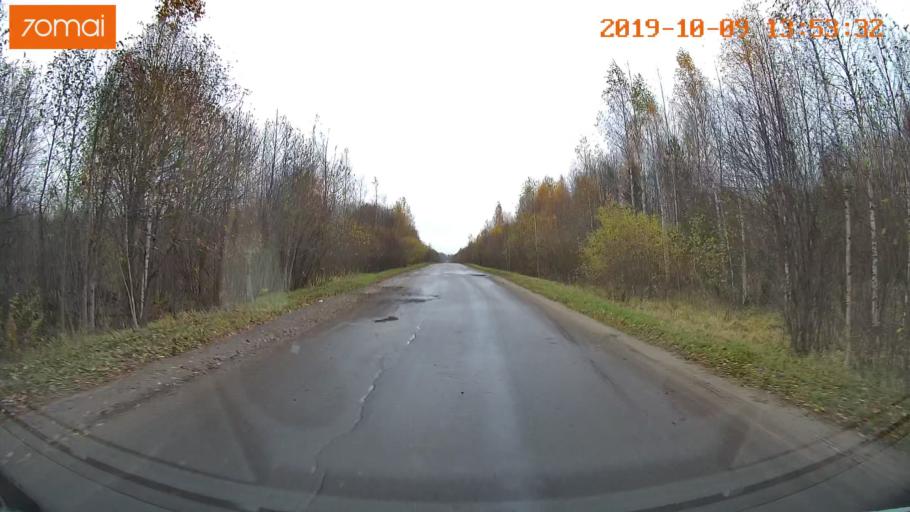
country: RU
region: Kostroma
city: Buy
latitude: 58.4161
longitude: 41.2591
